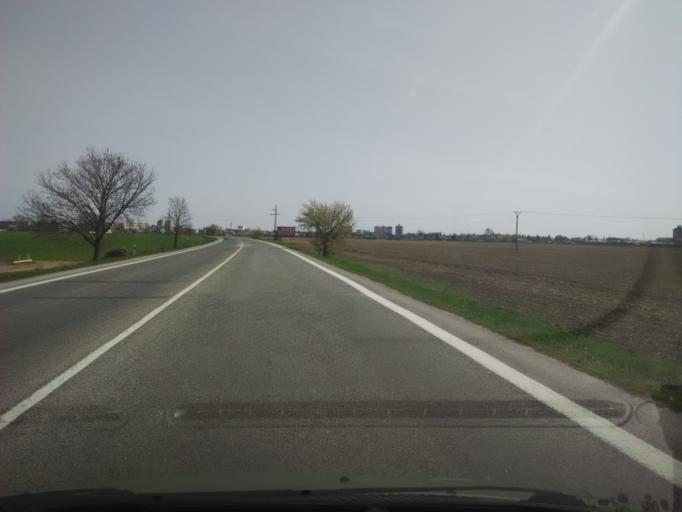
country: SK
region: Nitriansky
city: Sellye
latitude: 48.1593
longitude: 17.8503
